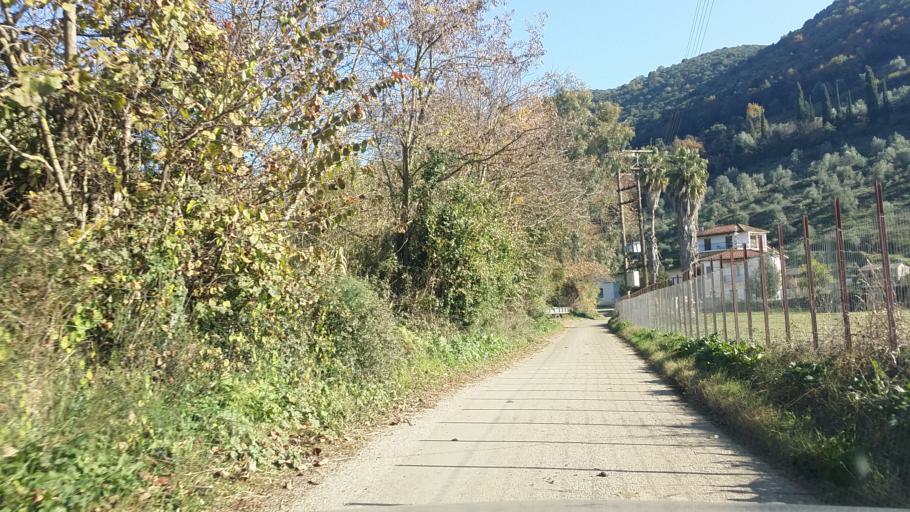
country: GR
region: West Greece
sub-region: Nomos Aitolias kai Akarnanias
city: Krikellos
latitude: 38.9613
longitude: 21.1921
